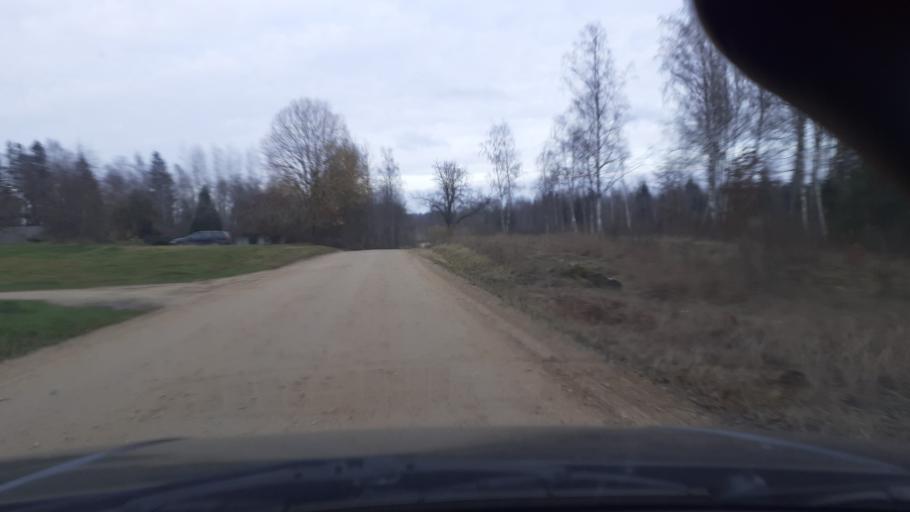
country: LV
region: Alsunga
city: Alsunga
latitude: 56.9494
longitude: 21.6425
